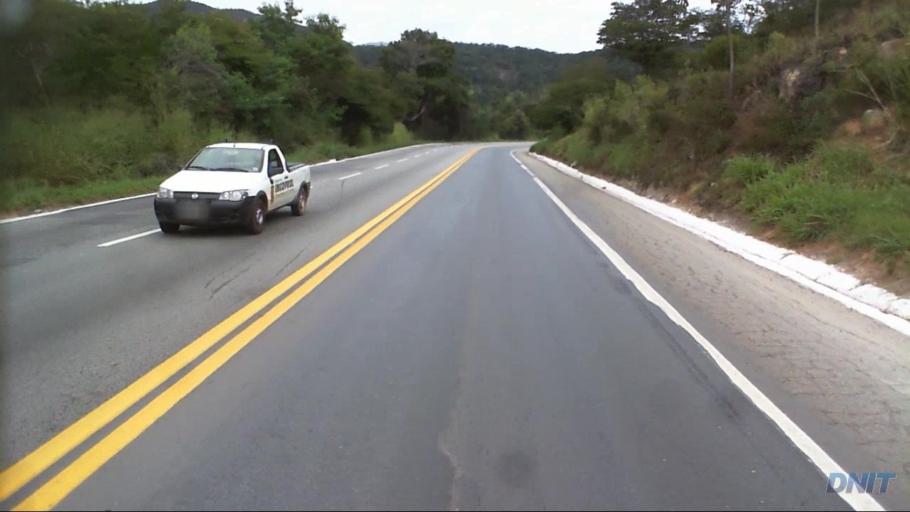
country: BR
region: Minas Gerais
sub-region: Caete
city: Caete
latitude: -19.7855
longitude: -43.7240
